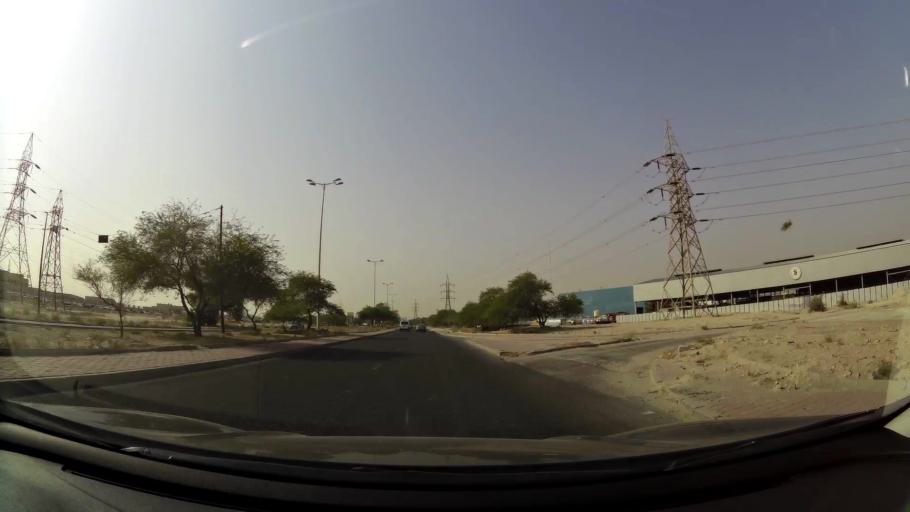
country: KW
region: Al Asimah
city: Ar Rabiyah
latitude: 29.2934
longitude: 47.8511
